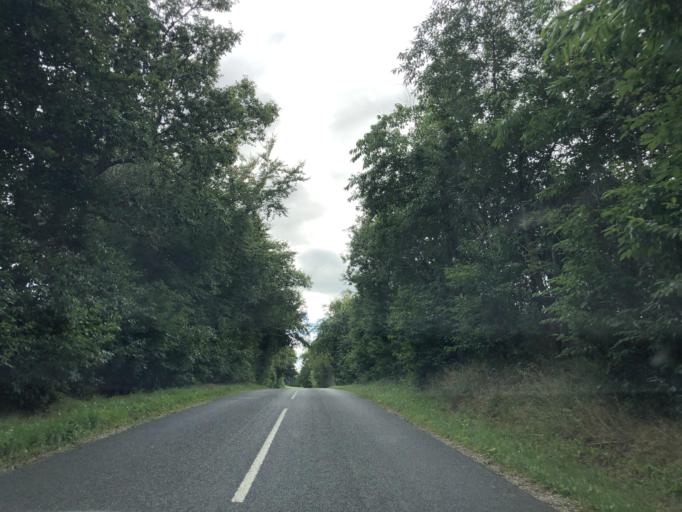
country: DK
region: North Denmark
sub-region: Vesthimmerland Kommune
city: Alestrup
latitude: 56.6008
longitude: 9.4327
